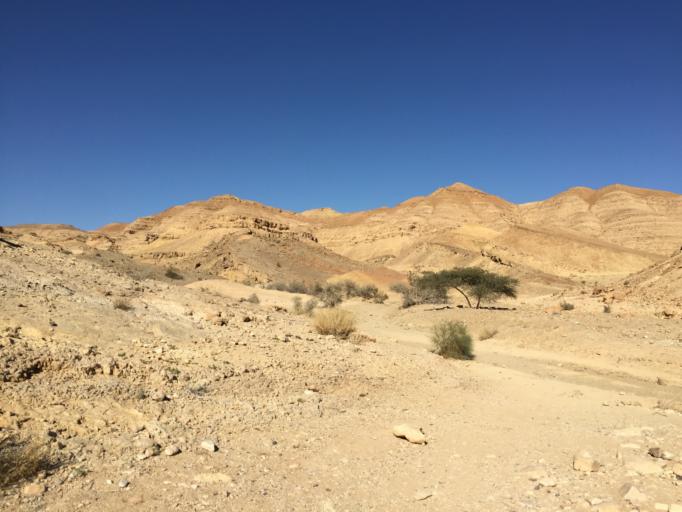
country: IL
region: Southern District
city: Mitzpe Ramon
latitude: 30.6024
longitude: 34.9491
